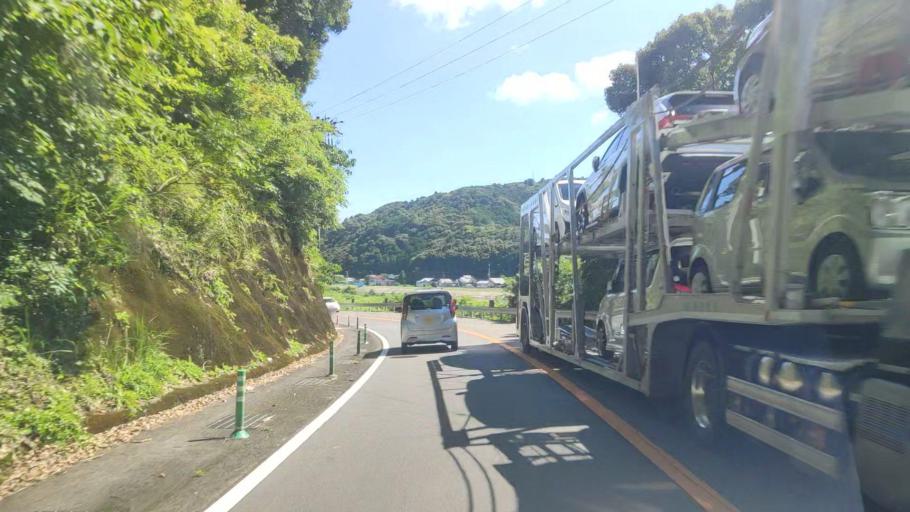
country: JP
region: Wakayama
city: Shingu
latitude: 33.5861
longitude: 135.9184
